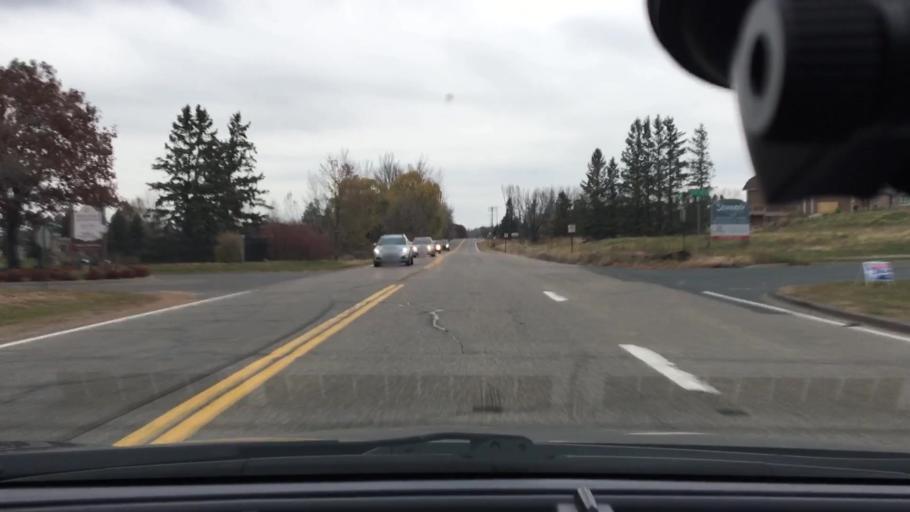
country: US
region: Minnesota
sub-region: Hennepin County
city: Corcoran
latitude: 45.0963
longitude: -93.5124
